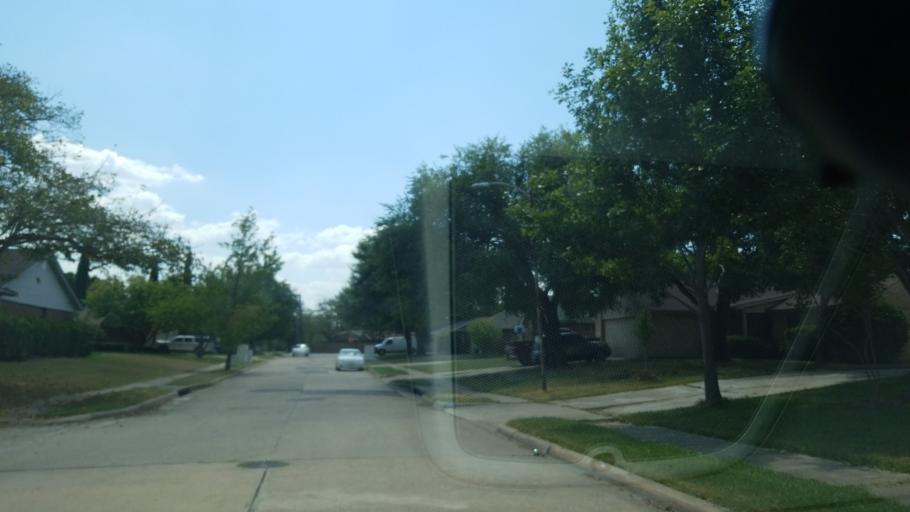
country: US
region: Texas
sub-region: Dallas County
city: Grand Prairie
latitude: 32.6999
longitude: -96.9980
